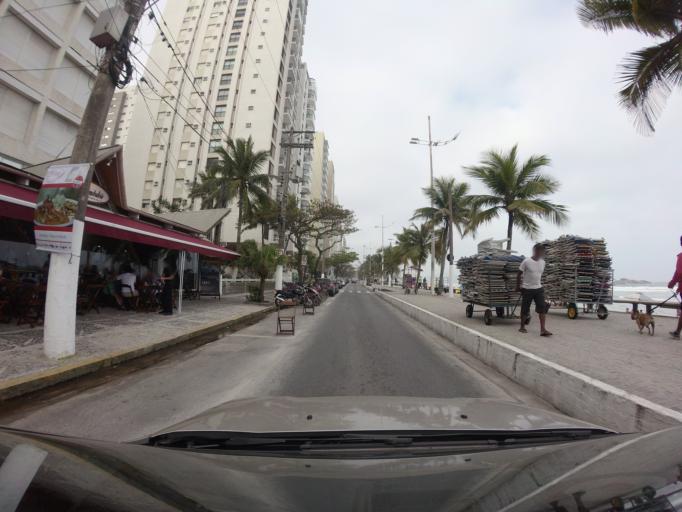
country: BR
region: Sao Paulo
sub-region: Guaruja
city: Guaruja
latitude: -23.9996
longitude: -46.2616
